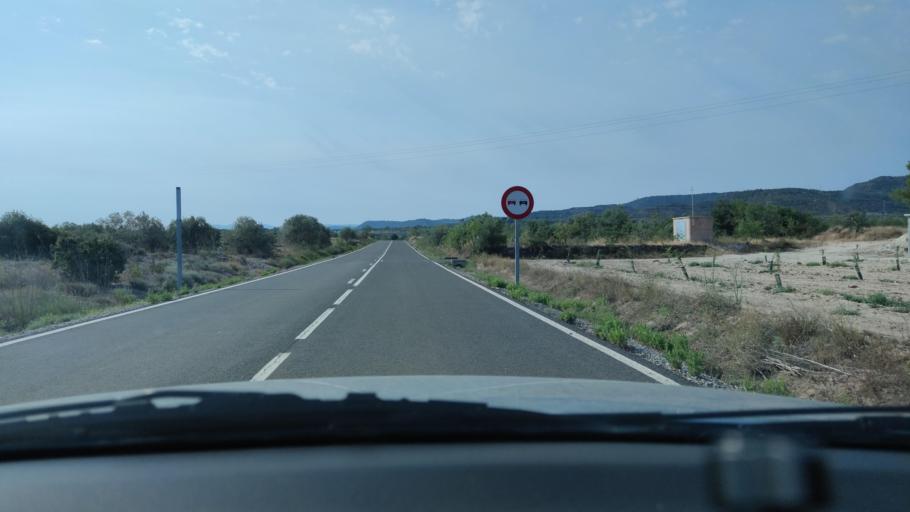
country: ES
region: Catalonia
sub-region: Provincia de Lleida
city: Arbeca
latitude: 41.4875
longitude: 0.8771
